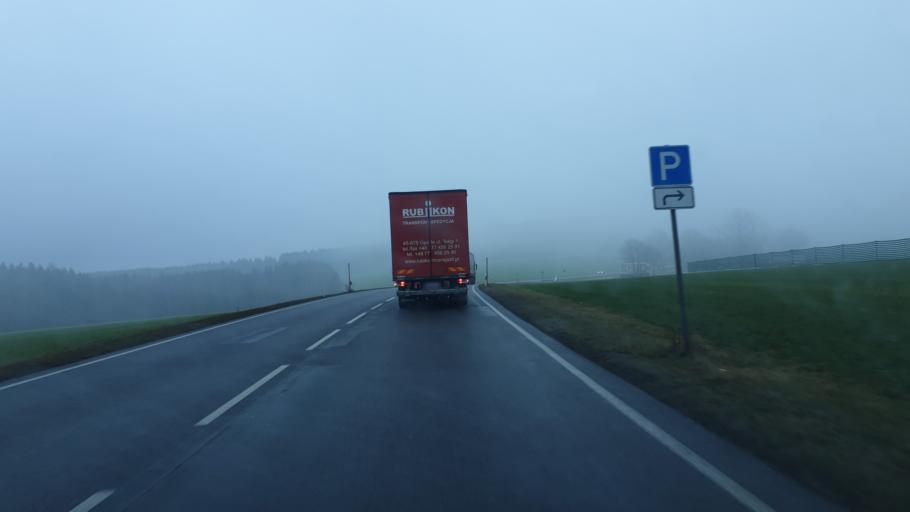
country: DE
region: Saxony
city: Grossolbersdorf
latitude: 50.7029
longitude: 13.1078
